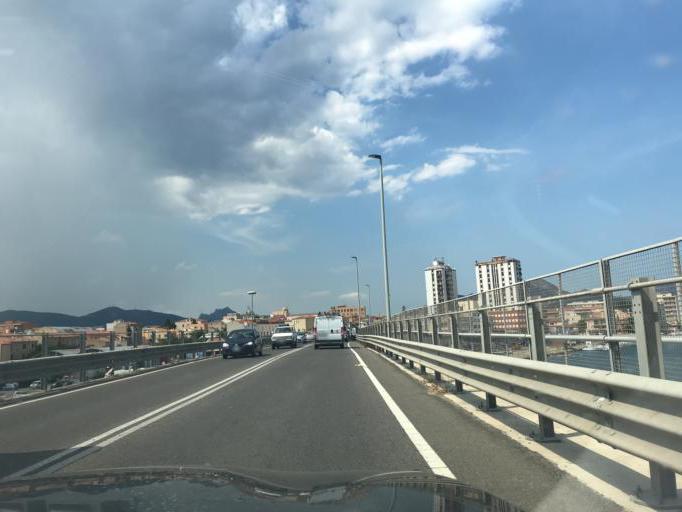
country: IT
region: Sardinia
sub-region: Provincia di Olbia-Tempio
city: Olbia
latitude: 40.9186
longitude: 9.5015
